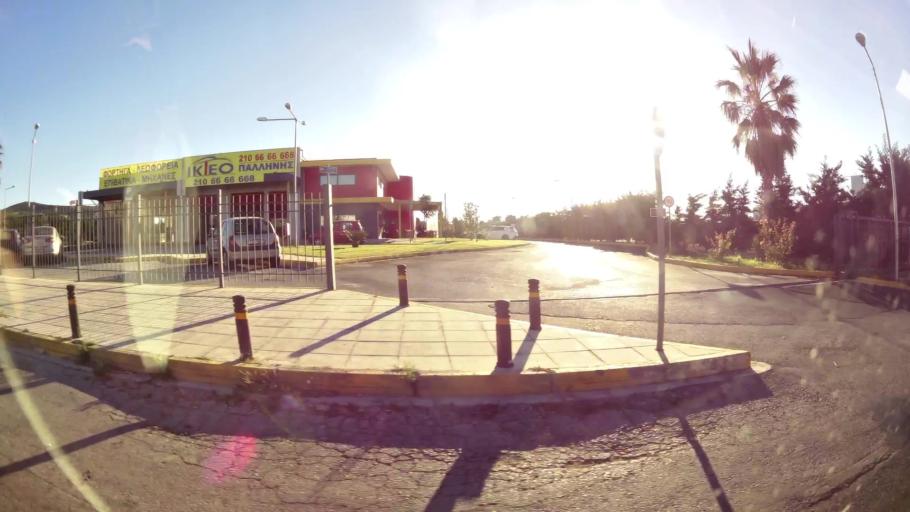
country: GR
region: Attica
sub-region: Nomarchia Anatolikis Attikis
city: Anthousa
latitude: 38.0115
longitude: 23.8713
